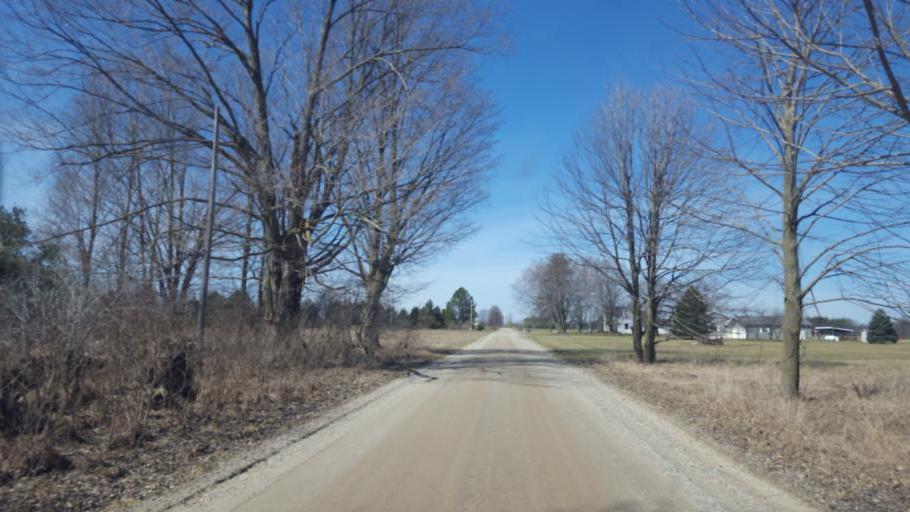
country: US
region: Michigan
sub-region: Montcalm County
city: Edmore
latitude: 43.4513
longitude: -85.0683
